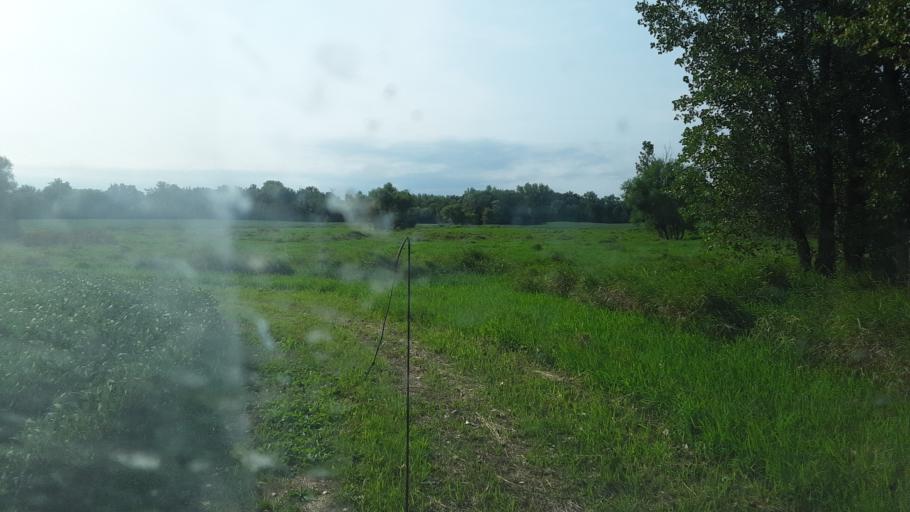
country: US
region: Ohio
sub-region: Crawford County
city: Bucyrus
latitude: 40.6637
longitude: -82.9567
